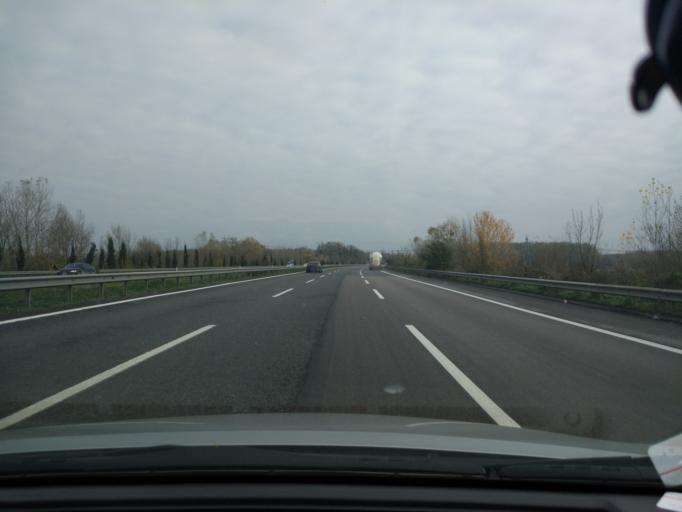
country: TR
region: Sakarya
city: Akyazi
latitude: 40.7335
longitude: 30.6401
